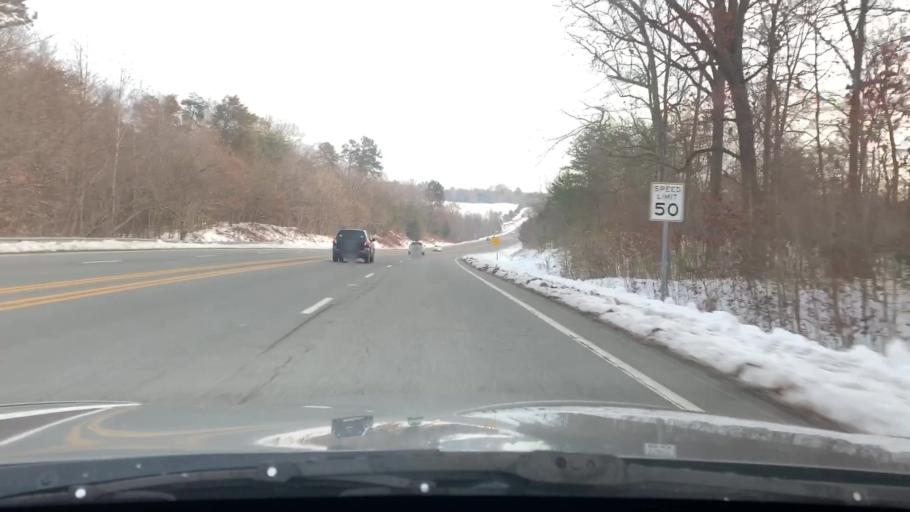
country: US
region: North Carolina
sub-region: Alamance County
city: Haw River
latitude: 36.0938
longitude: -79.3750
